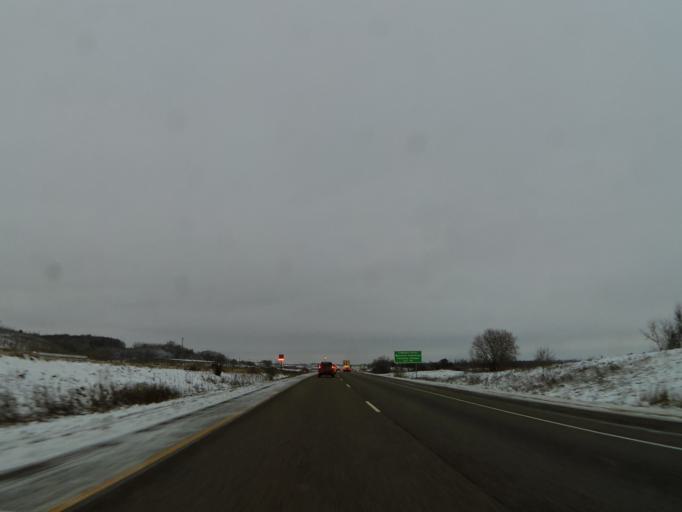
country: US
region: Wisconsin
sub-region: Saint Croix County
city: Roberts
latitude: 44.9509
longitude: -92.5439
